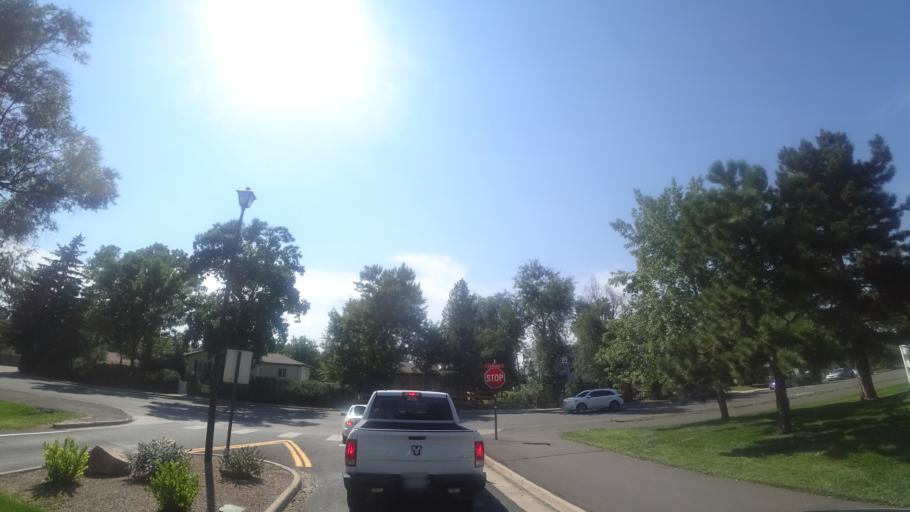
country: US
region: Colorado
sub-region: Arapahoe County
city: Englewood
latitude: 39.6390
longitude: -104.9782
